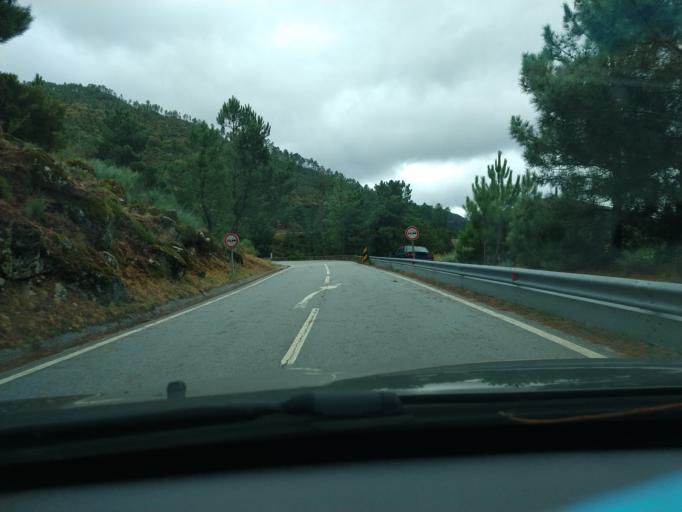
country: PT
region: Guarda
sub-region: Seia
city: Seia
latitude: 40.3259
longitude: -7.6793
